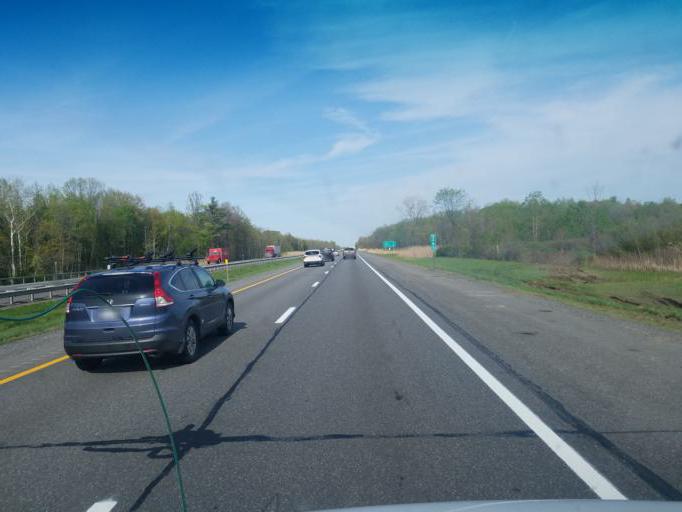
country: US
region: New York
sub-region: Madison County
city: Wampsville
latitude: 43.1021
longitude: -75.7213
